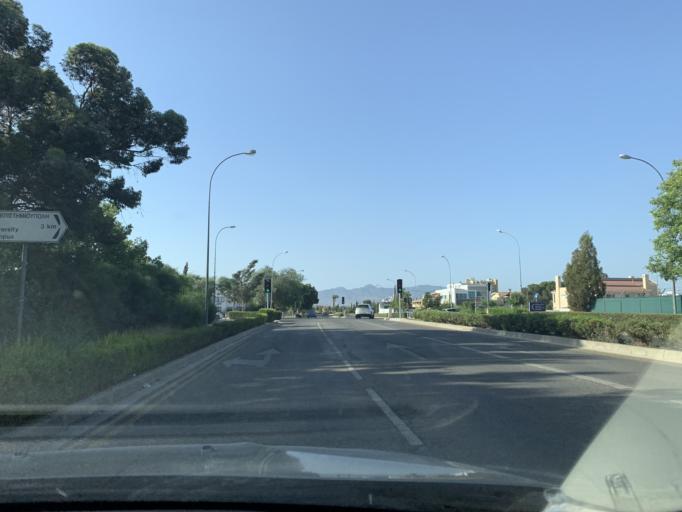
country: CY
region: Lefkosia
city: Nicosia
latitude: 35.1480
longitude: 33.3812
